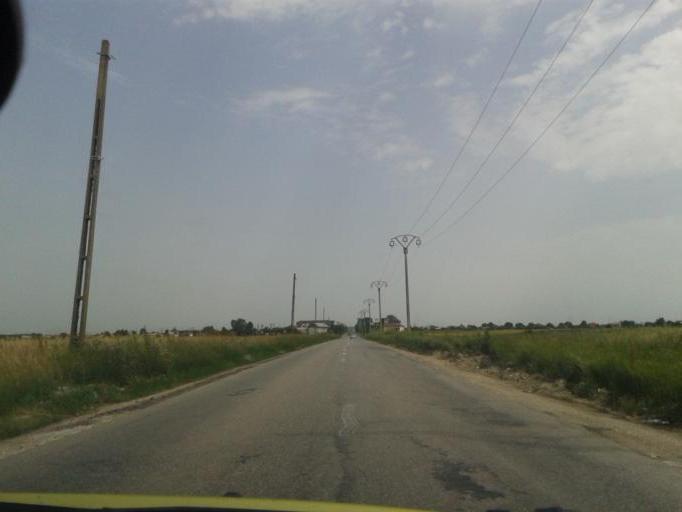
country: RO
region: Dambovita
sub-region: Comuna Petresti
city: Petresti
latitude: 44.6707
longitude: 25.3091
